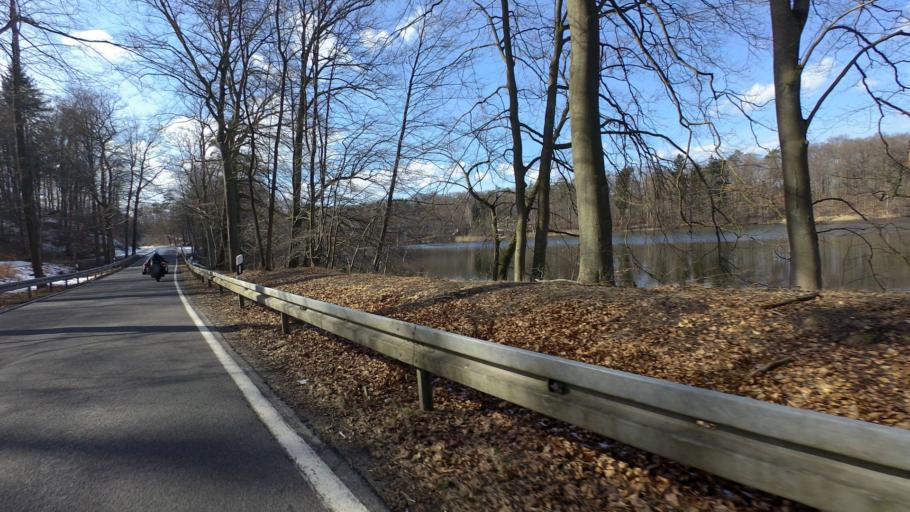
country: DE
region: Brandenburg
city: Rudnitz
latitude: 52.7589
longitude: 13.5504
